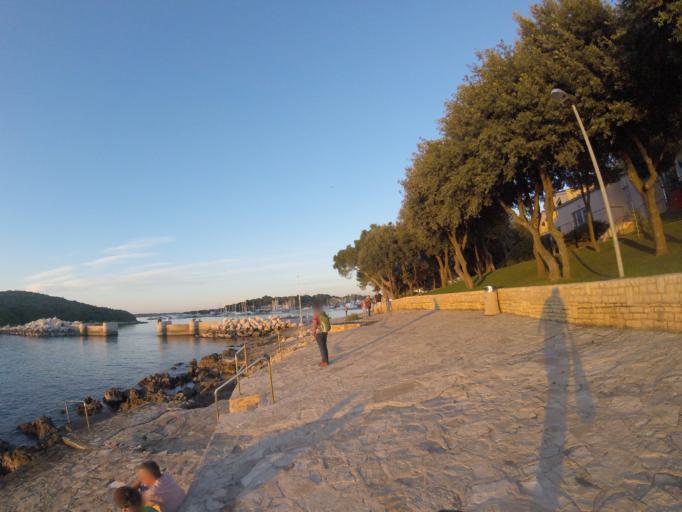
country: HR
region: Istarska
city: Vrsar
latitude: 45.1463
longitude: 13.5976
